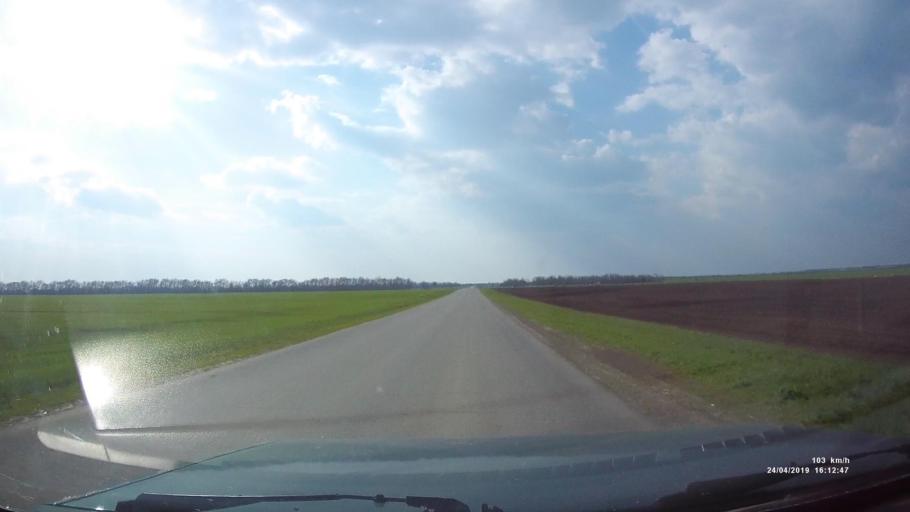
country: RU
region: Rostov
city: Sovetskoye
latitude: 46.7357
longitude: 42.2301
